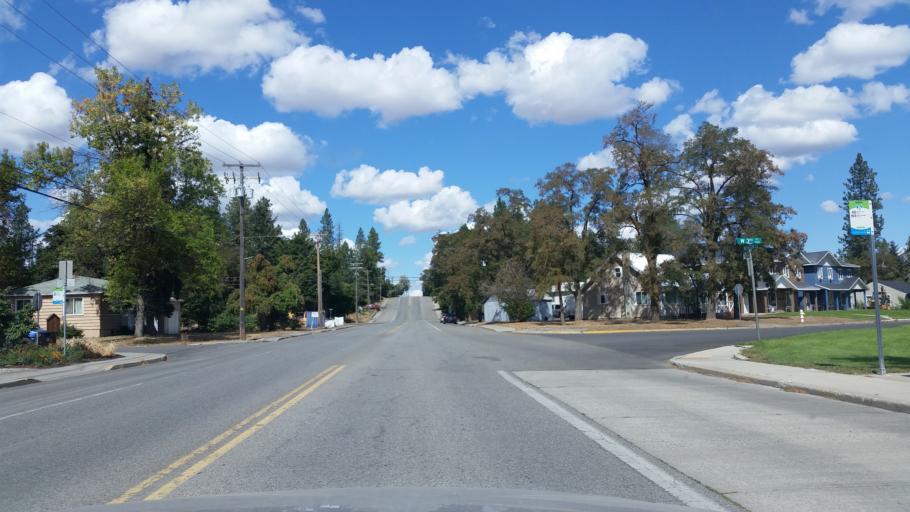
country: US
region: Washington
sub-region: Spokane County
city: Cheney
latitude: 47.4822
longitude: -117.5864
